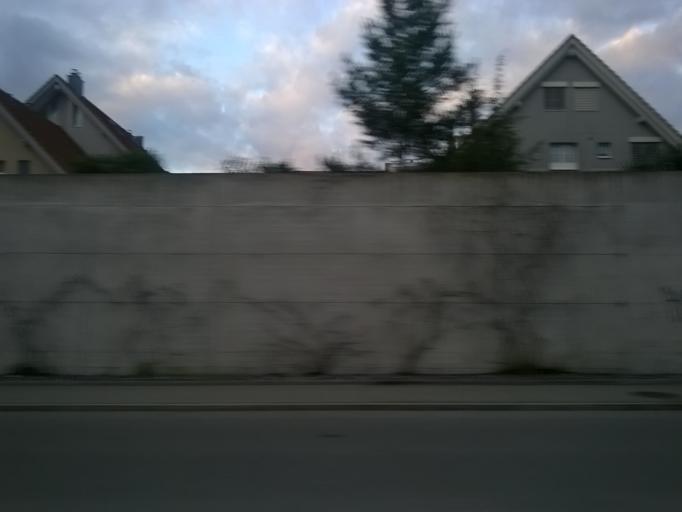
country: CH
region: Zurich
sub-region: Bezirk Buelach
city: Wallisellen / Wallisellen-West
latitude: 47.4165
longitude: 8.5801
